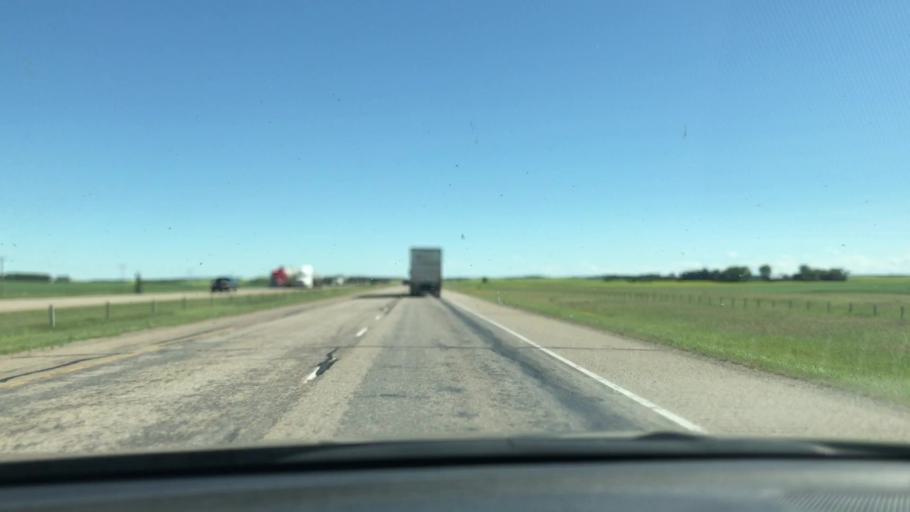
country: CA
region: Alberta
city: Olds
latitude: 51.8760
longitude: -114.0256
